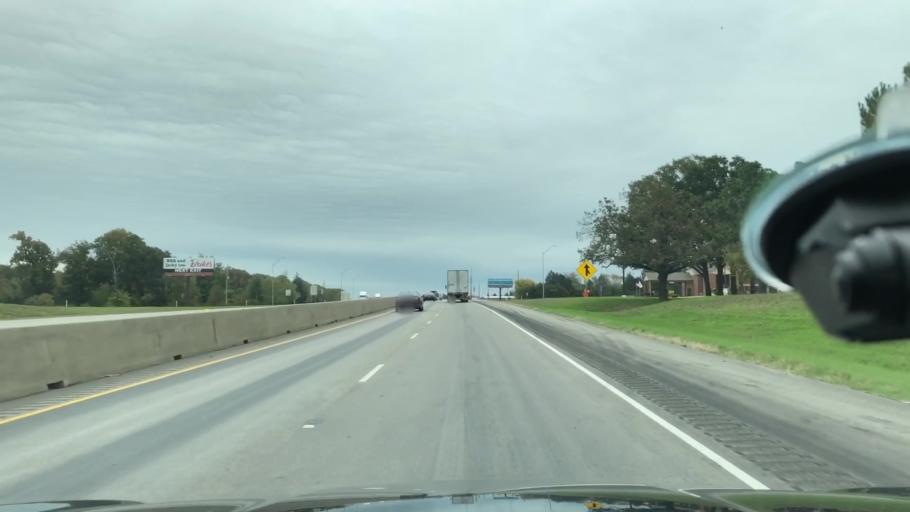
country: US
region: Texas
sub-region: Franklin County
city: Mount Vernon
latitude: 33.1616
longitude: -95.2336
